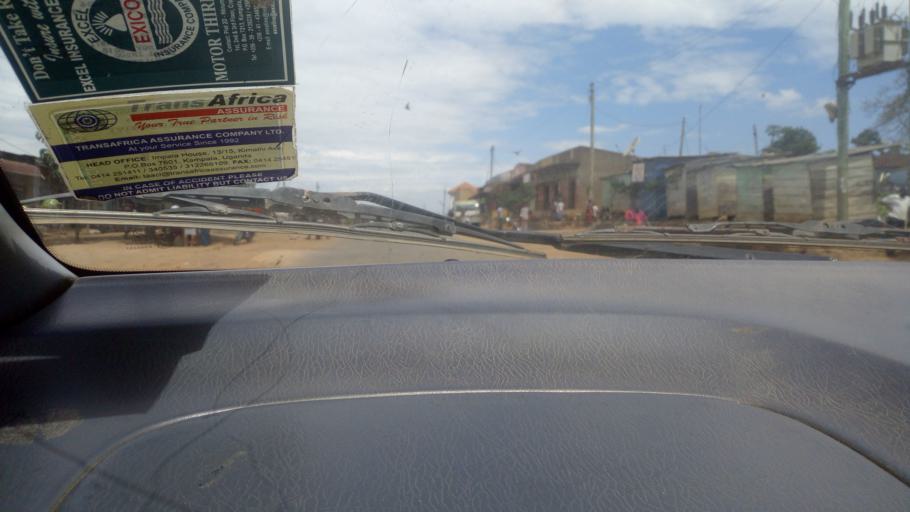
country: UG
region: Western Region
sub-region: Mbarara District
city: Bwizibwera
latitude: -0.4084
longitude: 30.5684
